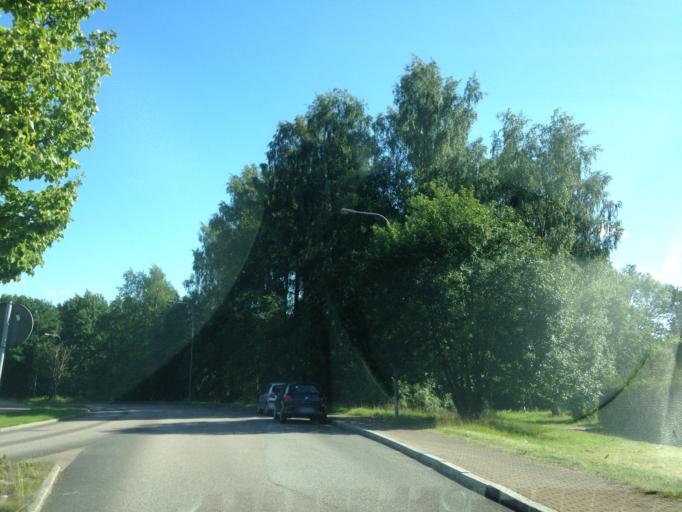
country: SE
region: Vaestra Goetaland
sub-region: Ale Kommun
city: Surte
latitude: 57.8041
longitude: 11.9742
